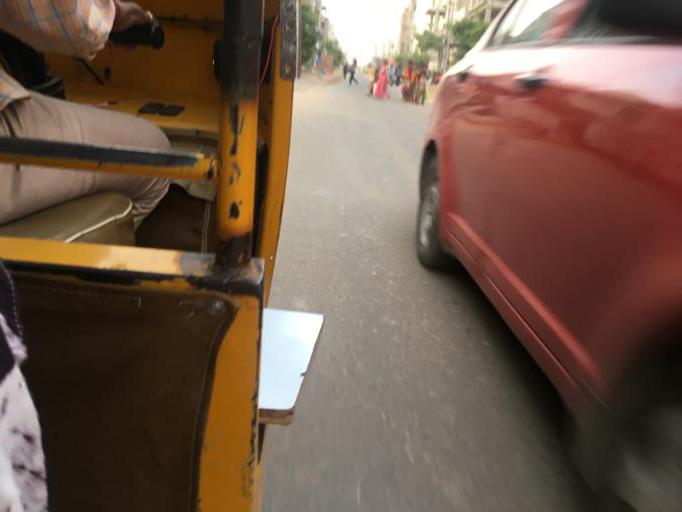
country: IN
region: Telangana
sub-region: Medak
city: Serilingampalle
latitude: 17.4311
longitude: 78.3333
